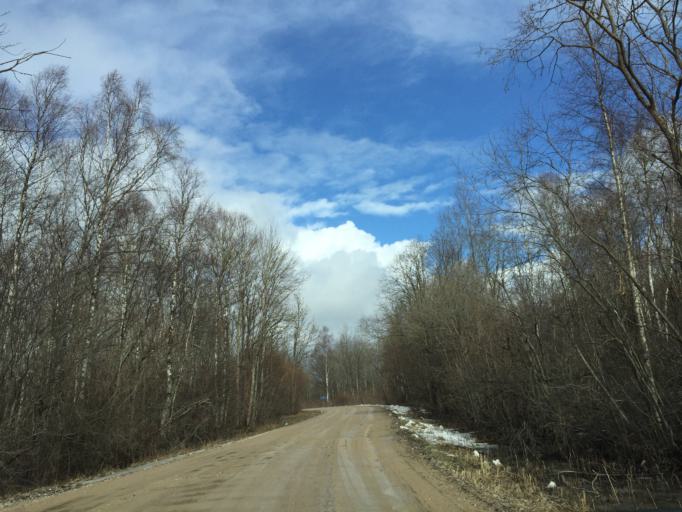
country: EE
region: Laeaene
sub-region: Lihula vald
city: Lihula
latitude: 58.7272
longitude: 23.8295
